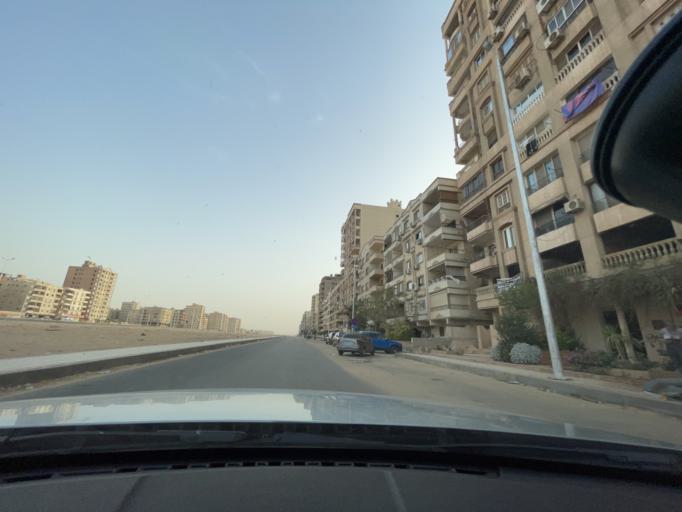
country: EG
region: Muhafazat al Qahirah
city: Cairo
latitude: 30.0544
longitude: 31.3714
